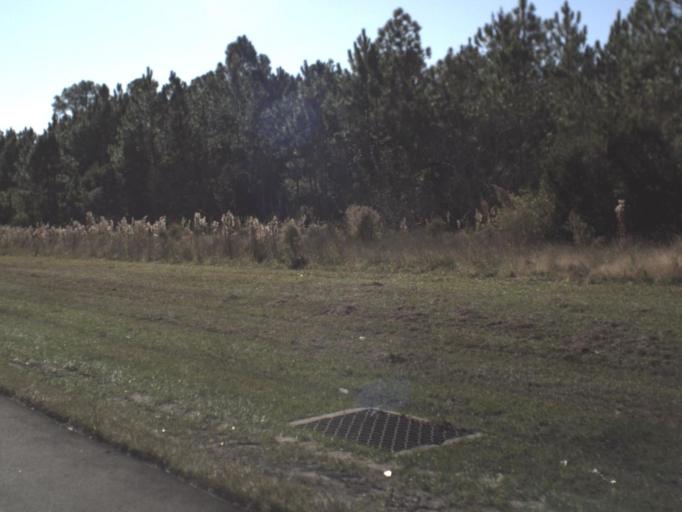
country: US
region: Florida
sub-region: Volusia County
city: Port Orange
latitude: 29.1331
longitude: -81.0487
